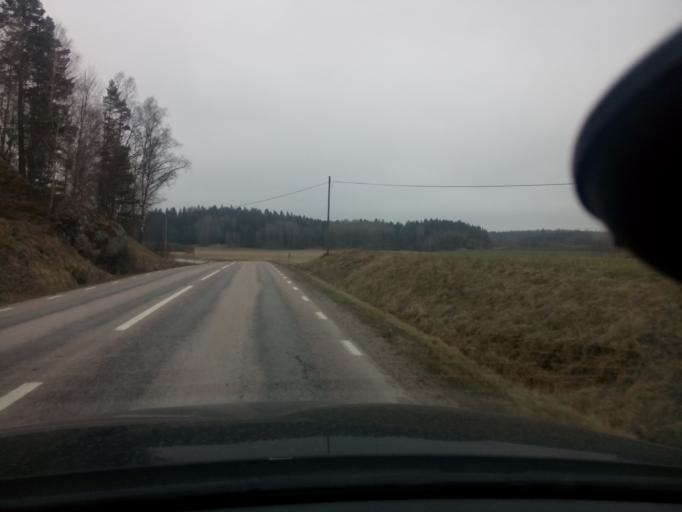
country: SE
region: Soedermanland
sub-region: Gnesta Kommun
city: Gnesta
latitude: 59.0398
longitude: 17.1611
